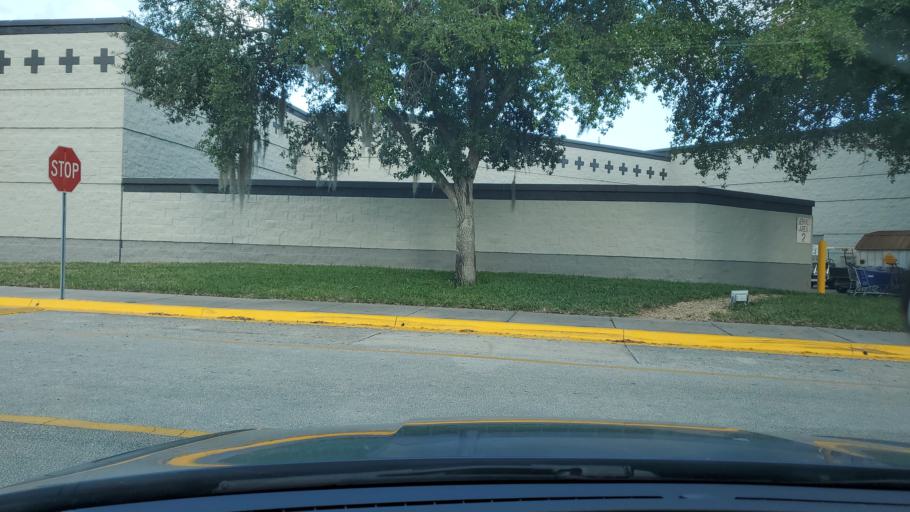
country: US
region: Florida
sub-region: Highlands County
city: Sebring
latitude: 27.4897
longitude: -81.4881
